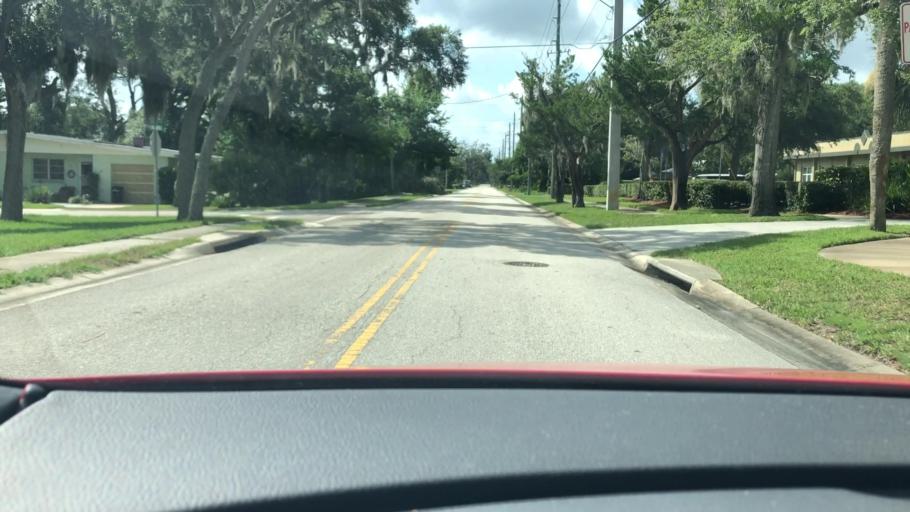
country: US
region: Florida
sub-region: Volusia County
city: Ormond Beach
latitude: 29.2756
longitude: -81.0545
